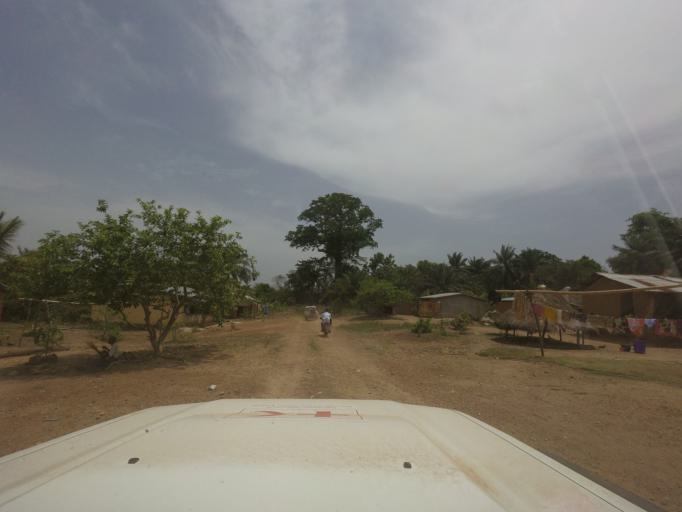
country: SL
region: Eastern Province
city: Buedu
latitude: 8.4843
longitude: -10.3343
